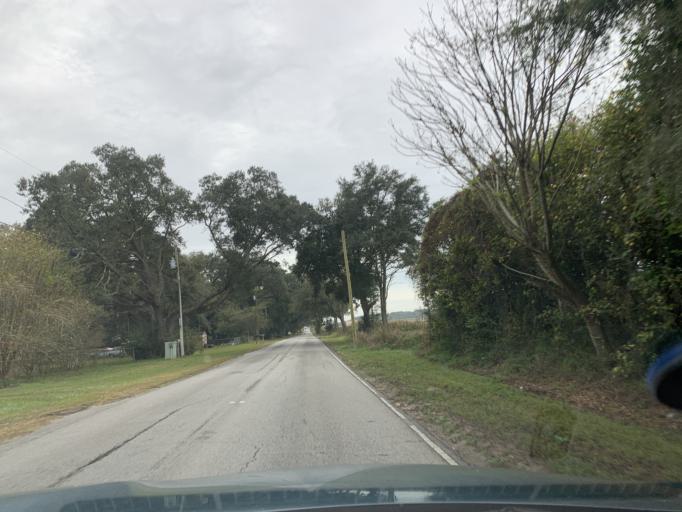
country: US
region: Florida
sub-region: Pasco County
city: Zephyrhills North
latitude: 28.2812
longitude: -82.1797
